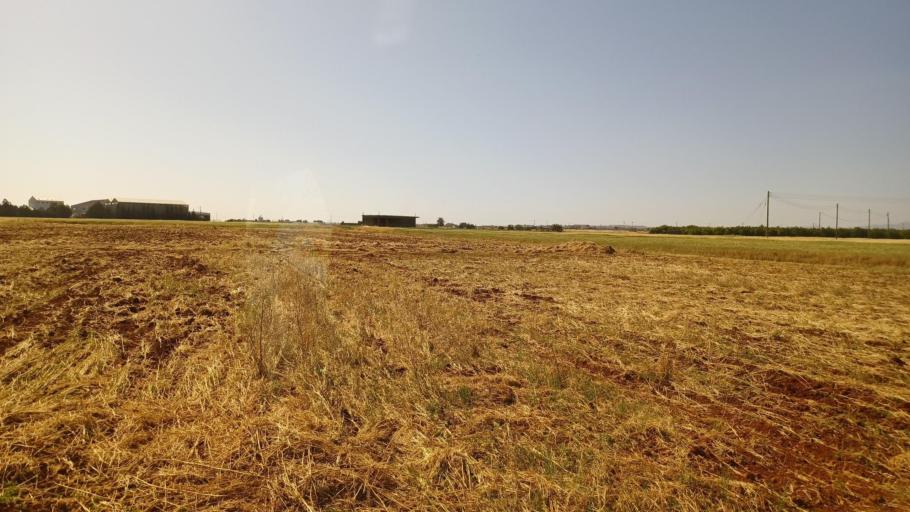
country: CY
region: Lefkosia
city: Kokkinotrimithia
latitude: 35.1471
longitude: 33.2182
